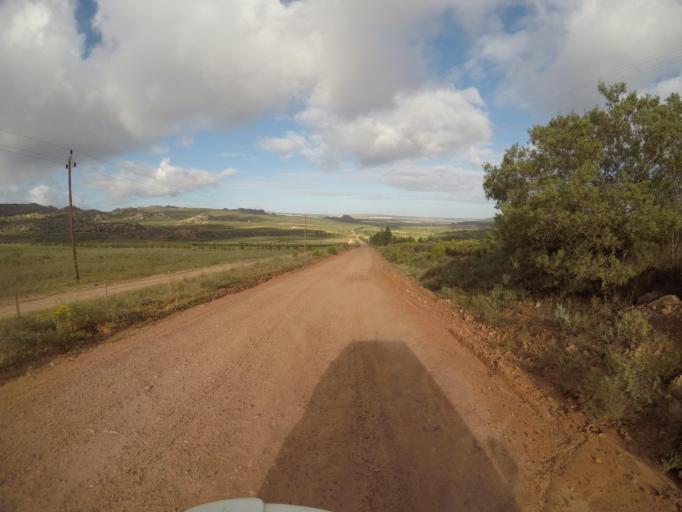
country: ZA
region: Western Cape
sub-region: West Coast District Municipality
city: Clanwilliam
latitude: -32.3440
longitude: 18.7561
